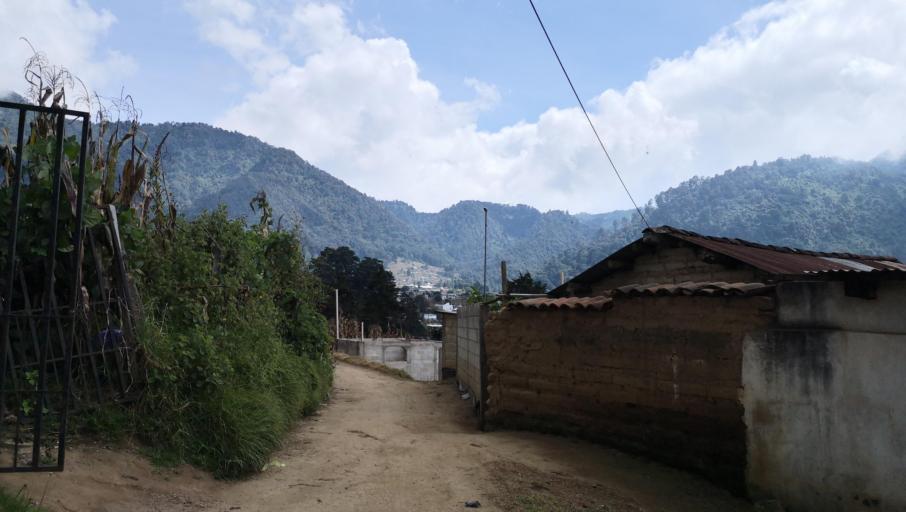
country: GT
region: Quetzaltenango
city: Cantel
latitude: 14.8174
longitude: -91.4414
